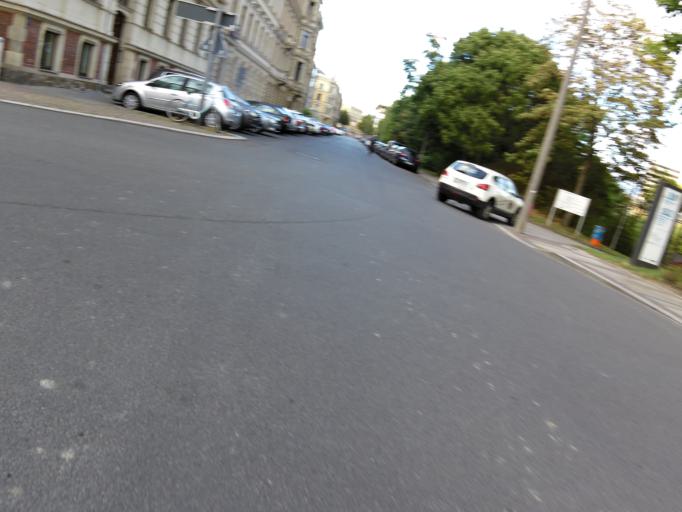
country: DE
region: Saxony
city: Leipzig
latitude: 51.3324
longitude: 12.3873
